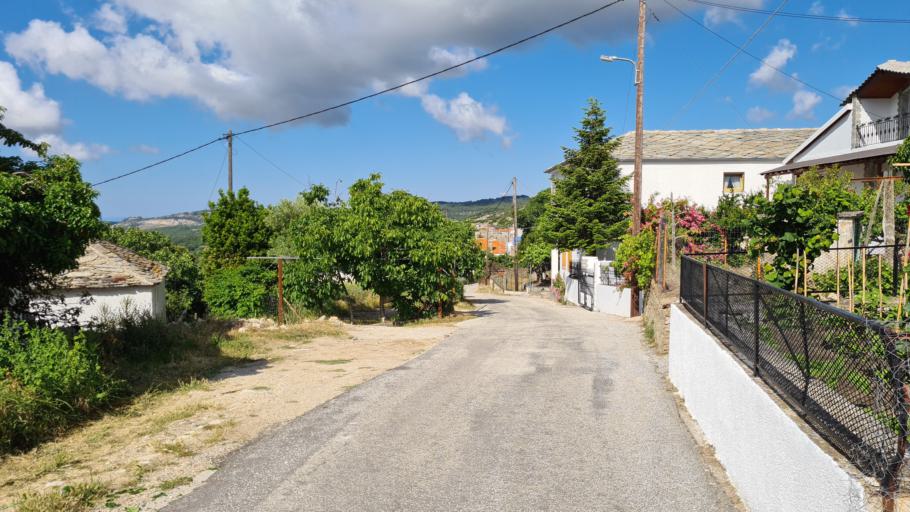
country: GR
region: East Macedonia and Thrace
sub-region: Nomos Kavalas
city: Potamia
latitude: 40.6620
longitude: 24.6999
